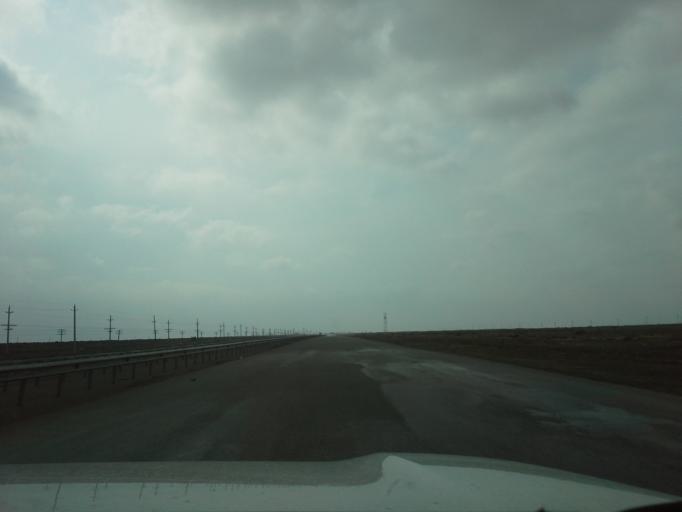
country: IR
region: Razavi Khorasan
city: Kalat-e Naderi
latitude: 37.2084
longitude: 60.0638
